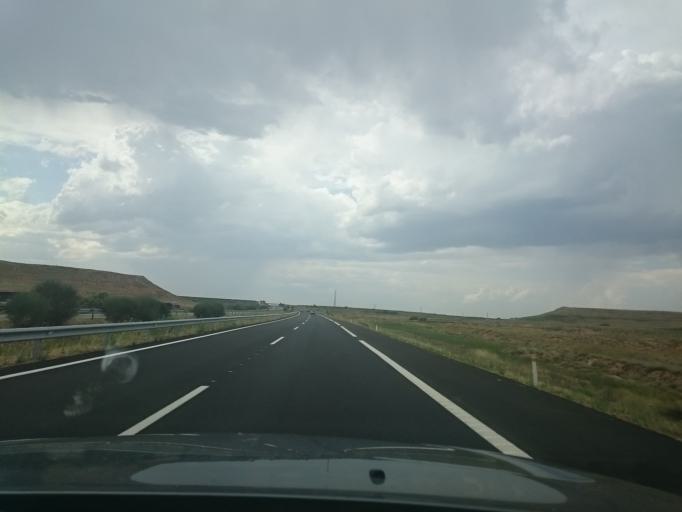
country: ES
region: La Rioja
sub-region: Provincia de La Rioja
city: Rincon de Soto
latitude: 42.2002
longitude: -1.8544
